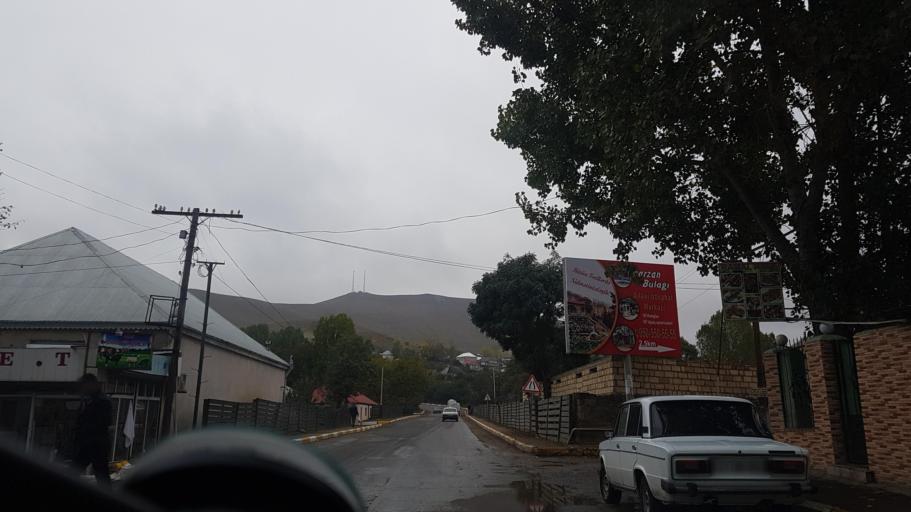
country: AZ
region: Gadabay Rayon
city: Ariqdam
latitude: 40.6577
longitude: 45.8078
